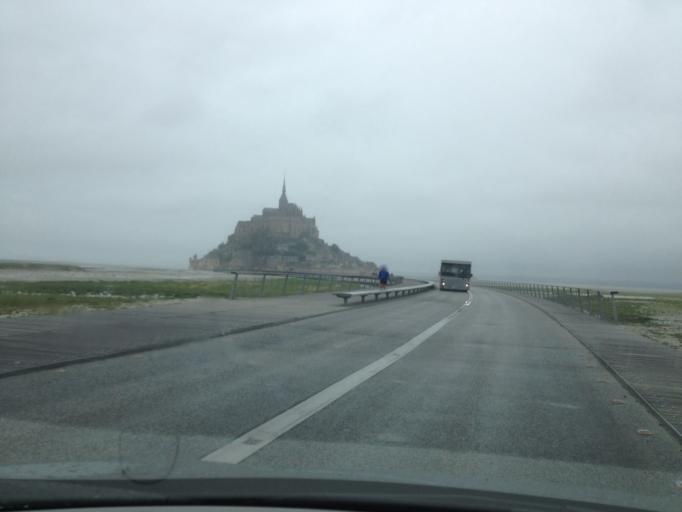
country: FR
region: Lower Normandy
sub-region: Departement de la Manche
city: Pontorson
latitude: 48.6279
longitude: -1.5062
